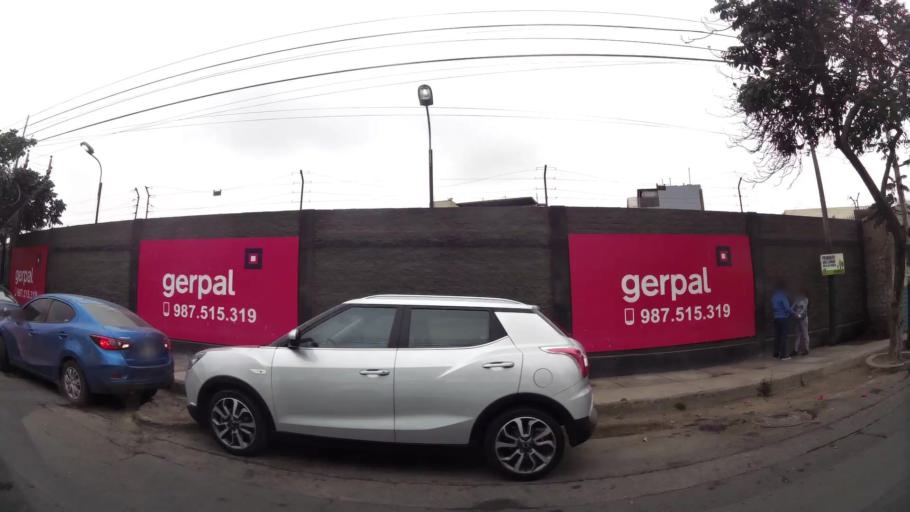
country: PE
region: Lima
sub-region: Lima
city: La Molina
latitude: -12.0933
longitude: -76.9739
